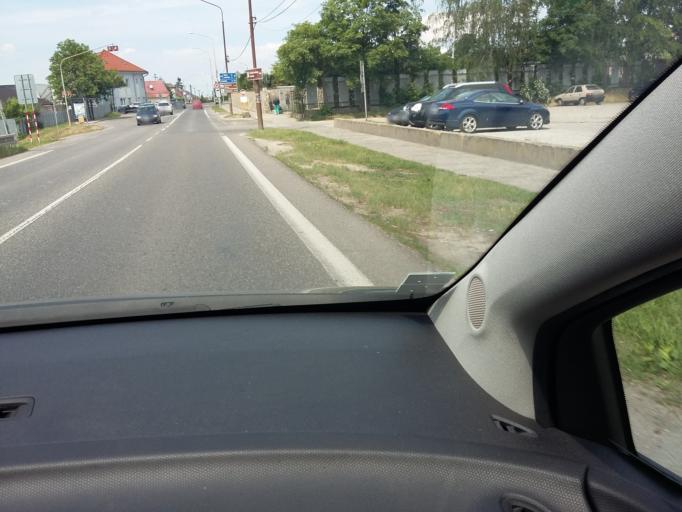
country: SK
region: Bratislavsky
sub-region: Okres Malacky
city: Malacky
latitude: 48.4390
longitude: 17.0252
